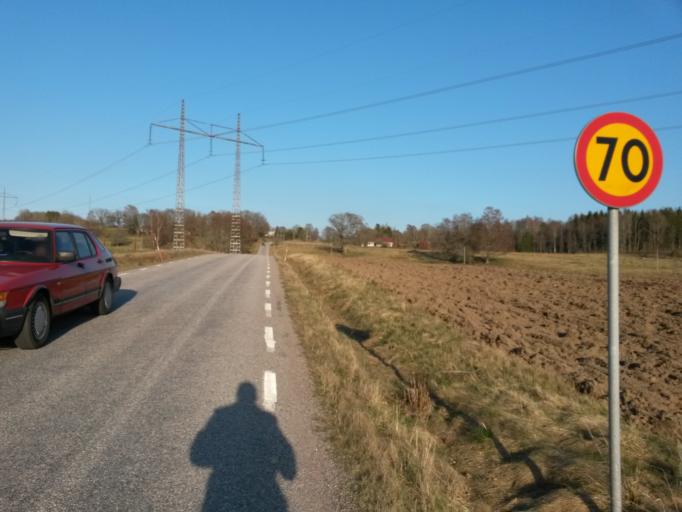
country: SE
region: Vaestra Goetaland
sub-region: Vargarda Kommun
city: Vargarda
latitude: 58.0156
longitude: 12.8183
